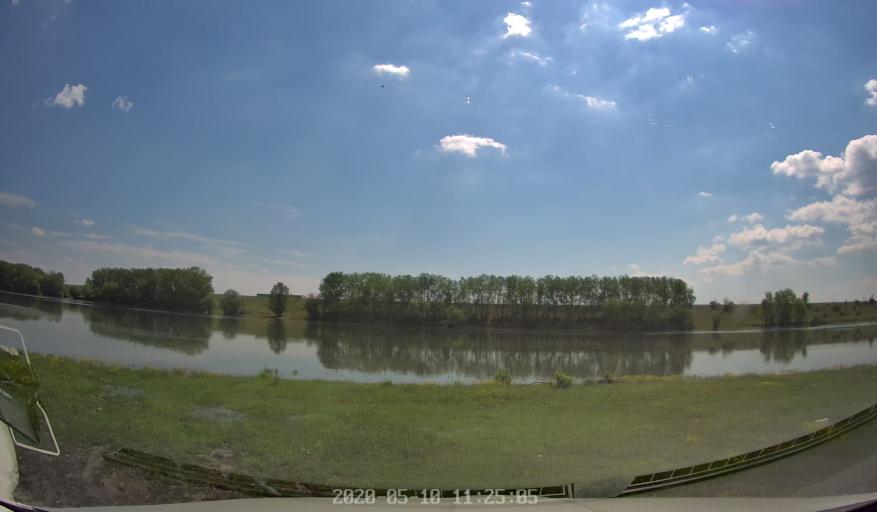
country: MD
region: Chisinau
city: Vadul lui Voda
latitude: 47.1294
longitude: 29.0886
